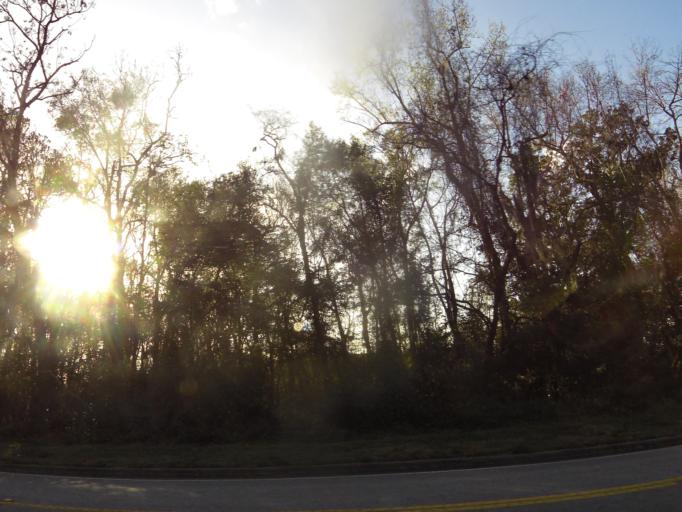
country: US
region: Florida
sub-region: Duval County
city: Jacksonville
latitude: 30.2624
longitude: -81.6033
